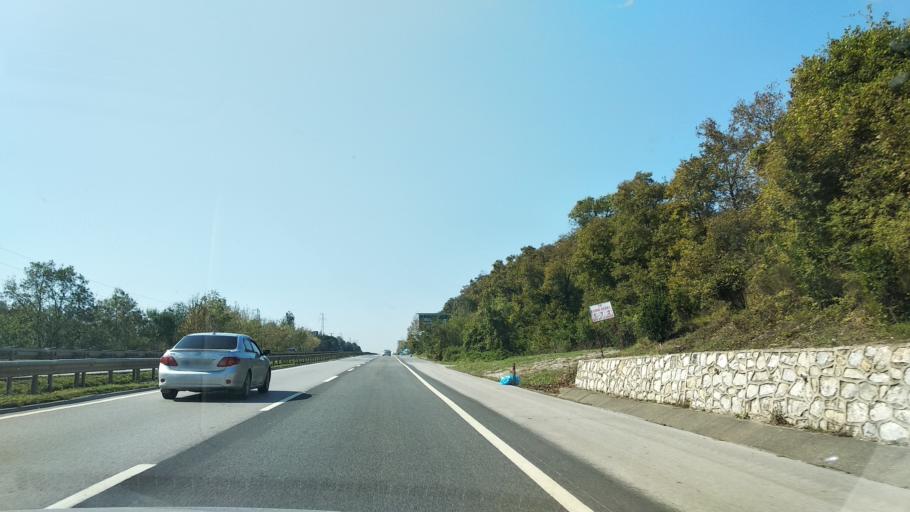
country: TR
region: Kocaeli
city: Derbent
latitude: 40.7315
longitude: 30.1676
